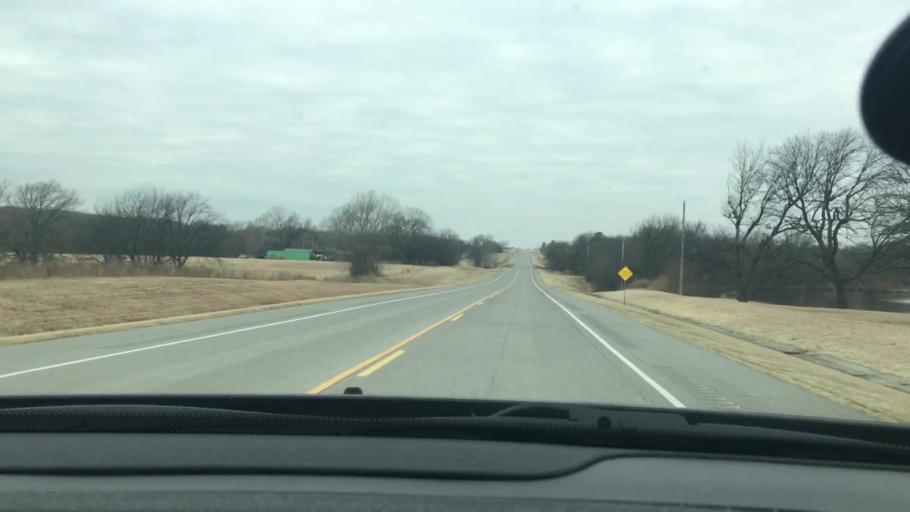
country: US
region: Oklahoma
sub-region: Murray County
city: Davis
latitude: 34.4925
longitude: -97.3757
